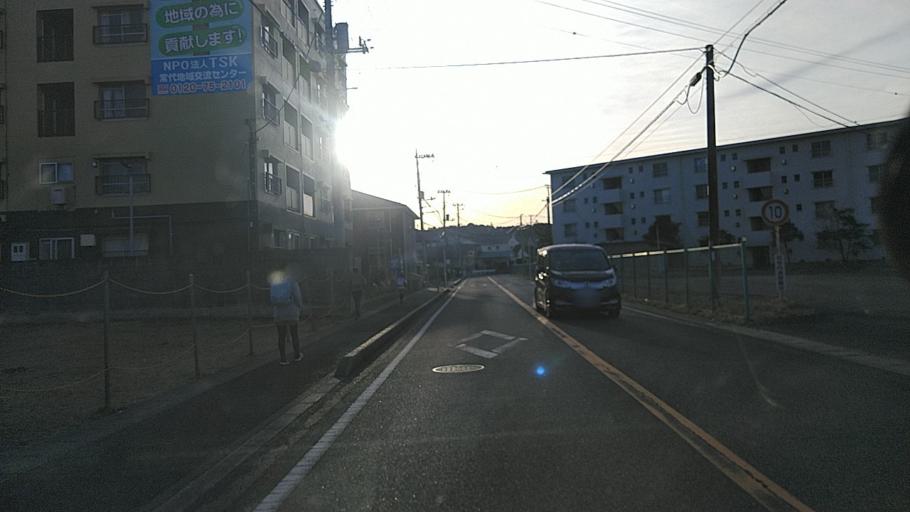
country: JP
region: Chiba
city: Kimitsu
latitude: 35.3063
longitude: 139.9238
